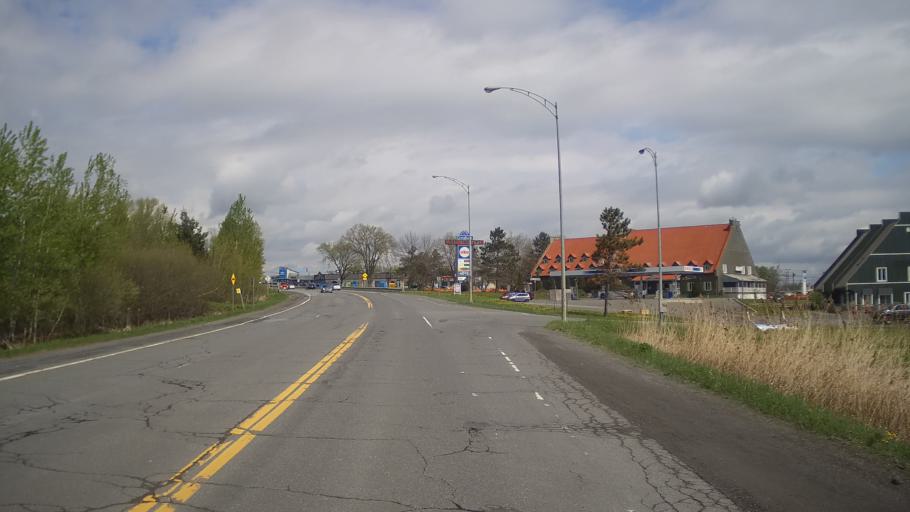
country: CA
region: Quebec
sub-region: Monteregie
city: Cowansville
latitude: 45.2077
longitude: -72.7678
